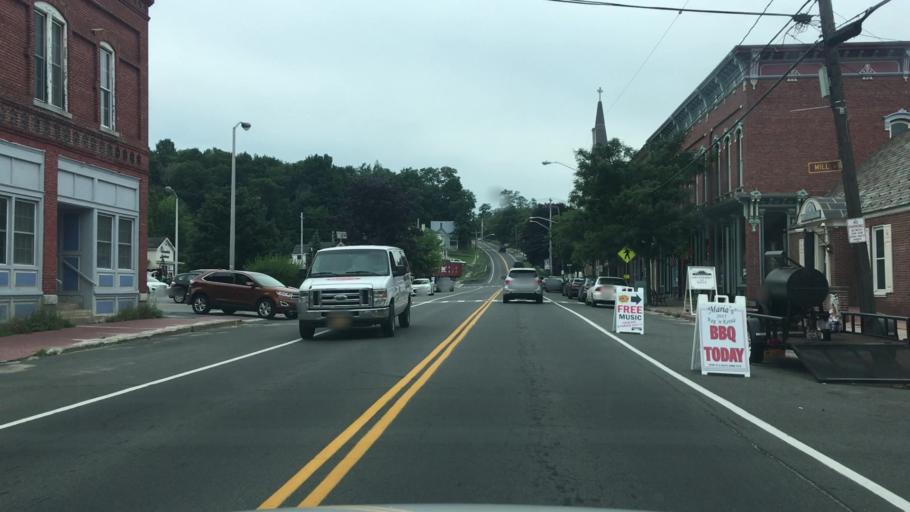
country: US
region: New York
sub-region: Essex County
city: Keeseville
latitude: 44.5046
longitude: -73.4803
